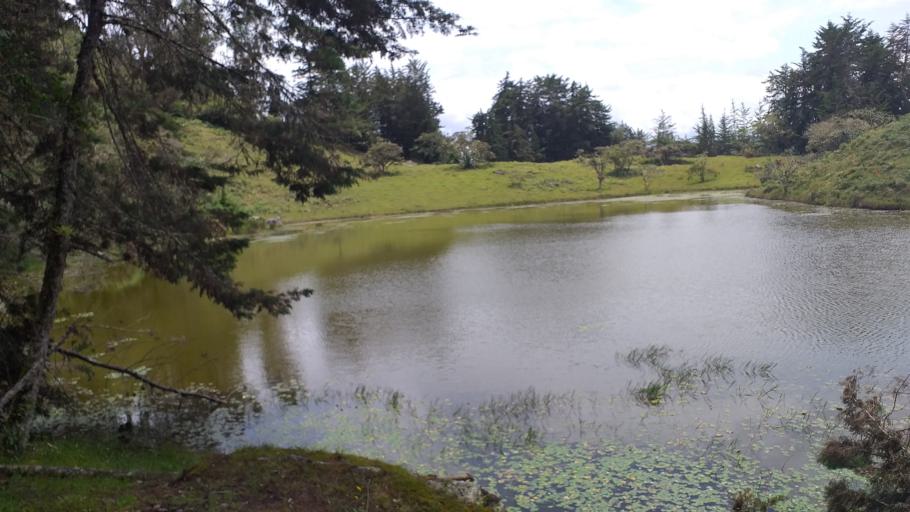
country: CO
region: Cundinamarca
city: Tenza
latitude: 5.0724
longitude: -73.4563
